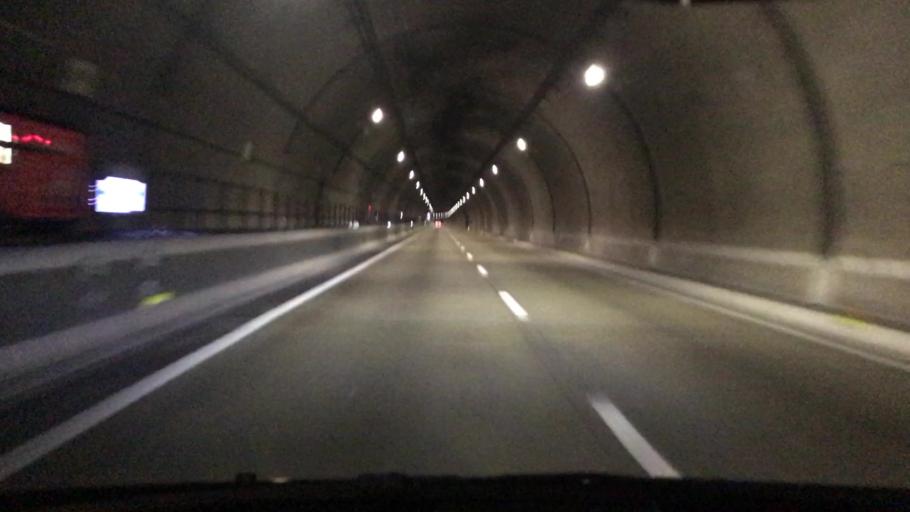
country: JP
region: Hyogo
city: Sandacho
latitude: 34.8024
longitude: 135.2404
